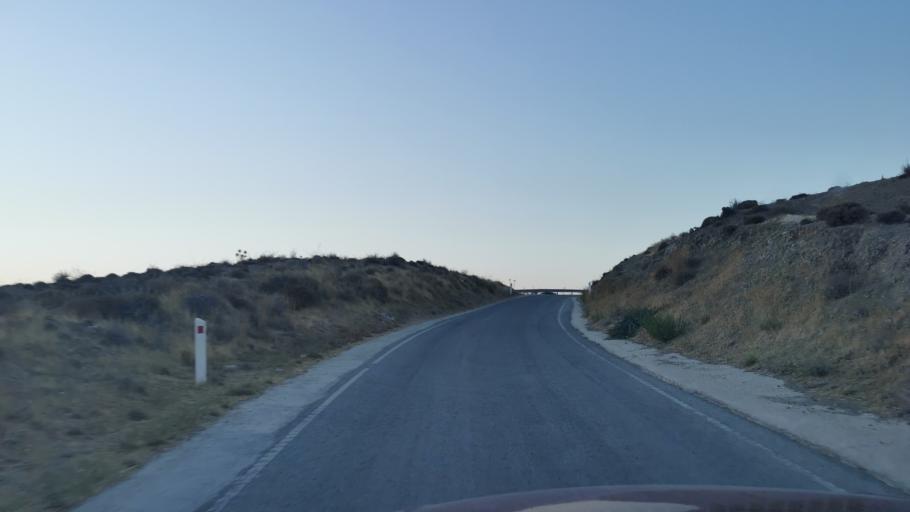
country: CY
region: Lefkosia
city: Peristerona
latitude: 35.0724
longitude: 33.0806
